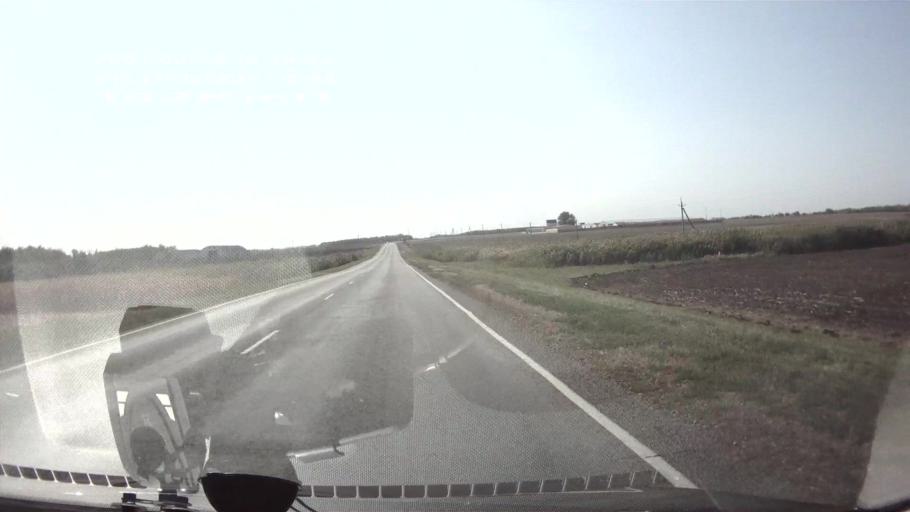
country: RU
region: Krasnodarskiy
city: Dmitriyevskaya
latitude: 45.7523
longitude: 40.7191
